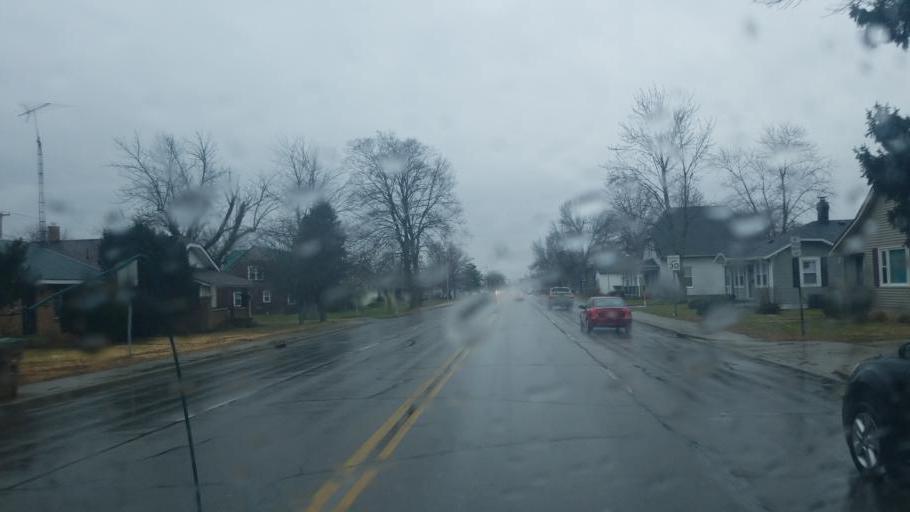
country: US
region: Indiana
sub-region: Bartholomew County
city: Columbus
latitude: 39.2190
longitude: -85.9042
